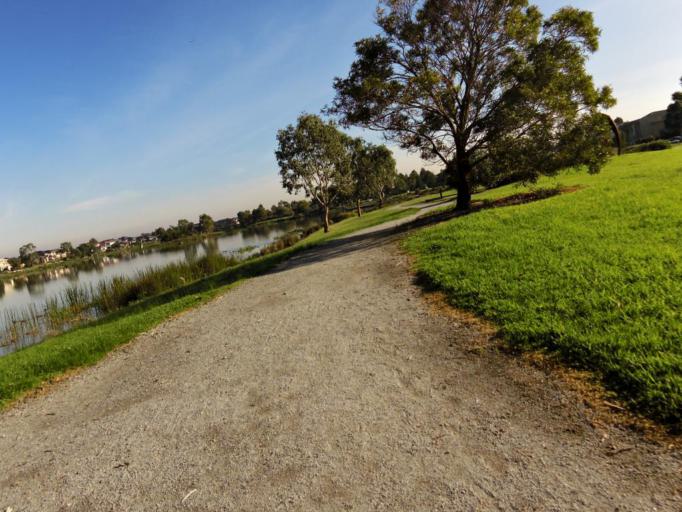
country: AU
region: Victoria
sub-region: Kingston
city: Waterways
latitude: -38.0147
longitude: 145.1329
